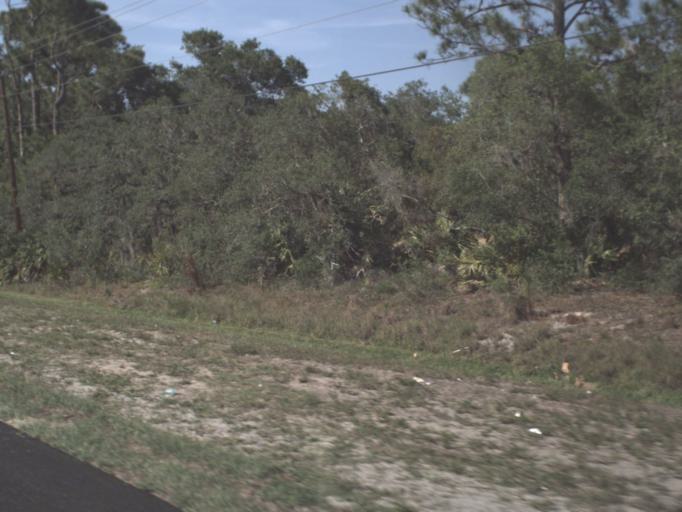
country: US
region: Florida
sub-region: Brevard County
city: Port Saint John
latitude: 28.5386
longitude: -80.7929
